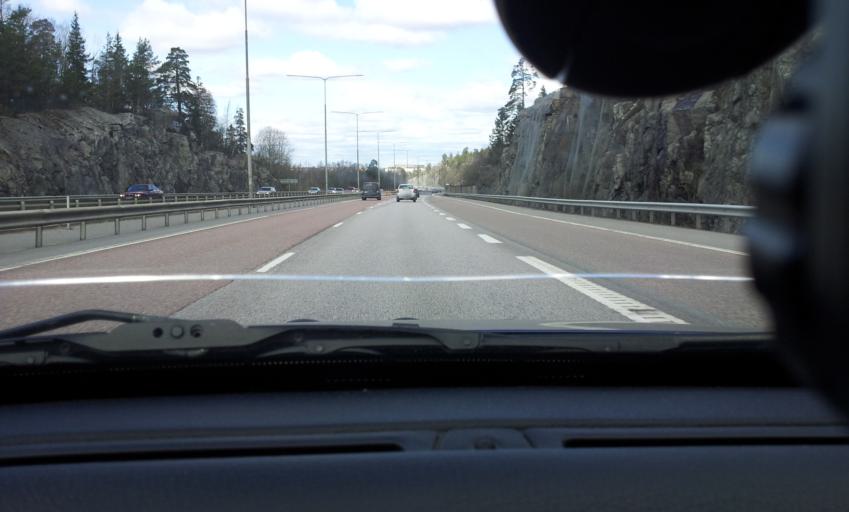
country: SE
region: Stockholm
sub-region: Haninge Kommun
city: Handen
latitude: 59.2319
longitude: 18.1240
